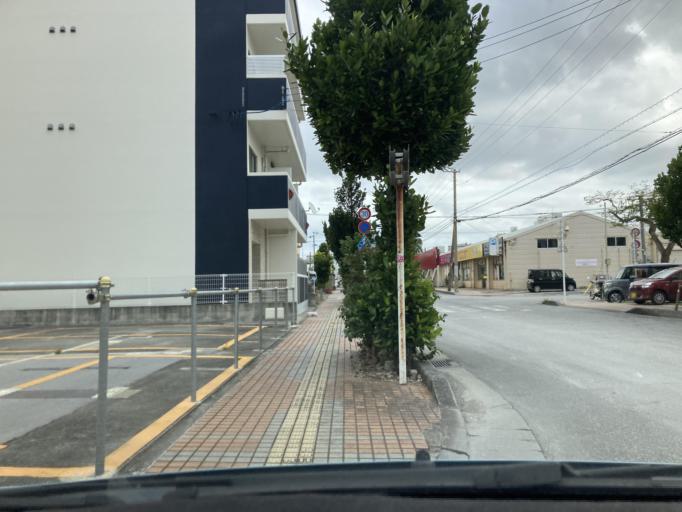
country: JP
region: Okinawa
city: Naha-shi
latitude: 26.2158
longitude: 127.6668
